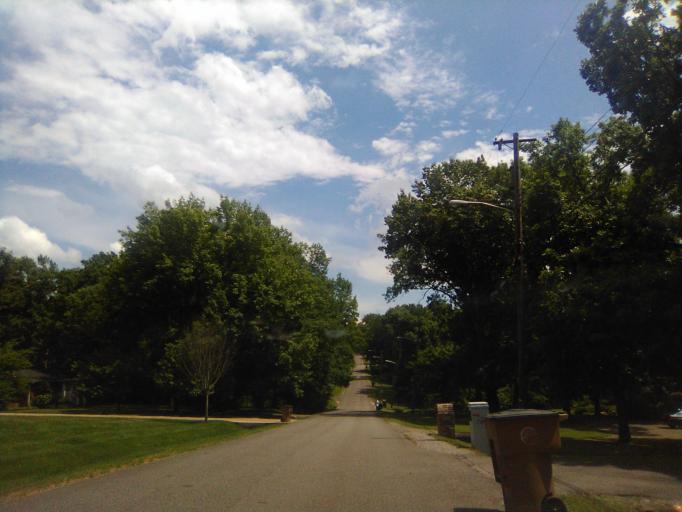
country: US
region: Tennessee
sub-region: Davidson County
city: Belle Meade
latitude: 36.1236
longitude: -86.8806
